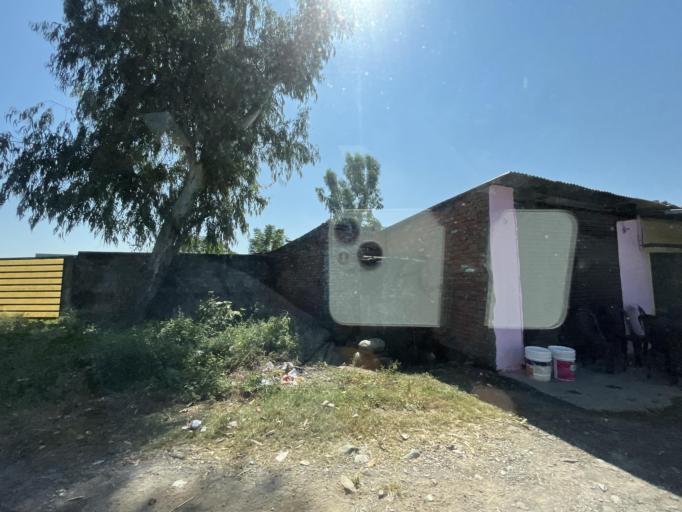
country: IN
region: Uttarakhand
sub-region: Naini Tal
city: Haldwani
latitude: 29.2113
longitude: 79.4695
